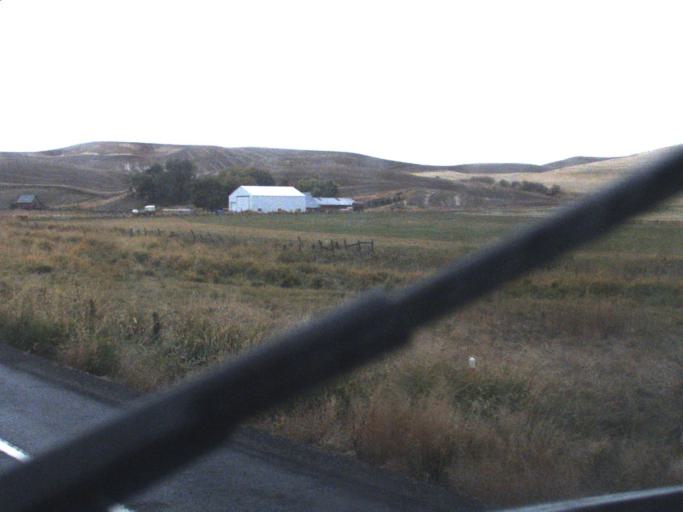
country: US
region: Washington
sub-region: Whitman County
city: Colfax
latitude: 46.8406
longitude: -117.3390
